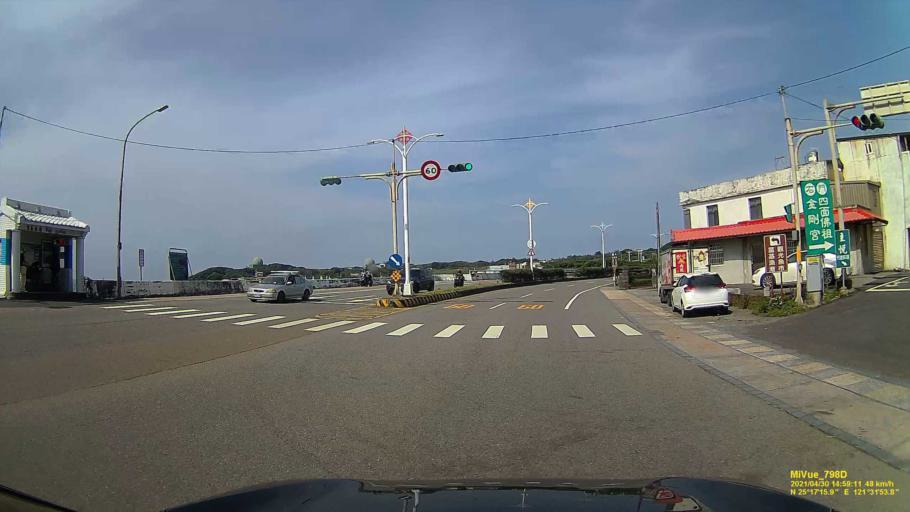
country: TW
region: Taipei
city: Taipei
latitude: 25.2880
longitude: 121.5319
